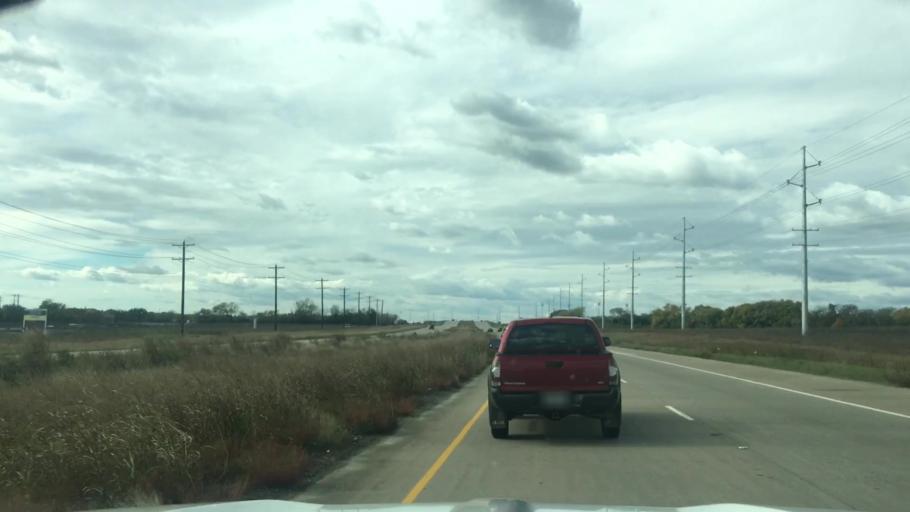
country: US
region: Texas
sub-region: Denton County
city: Denton
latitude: 33.2534
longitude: -97.1012
